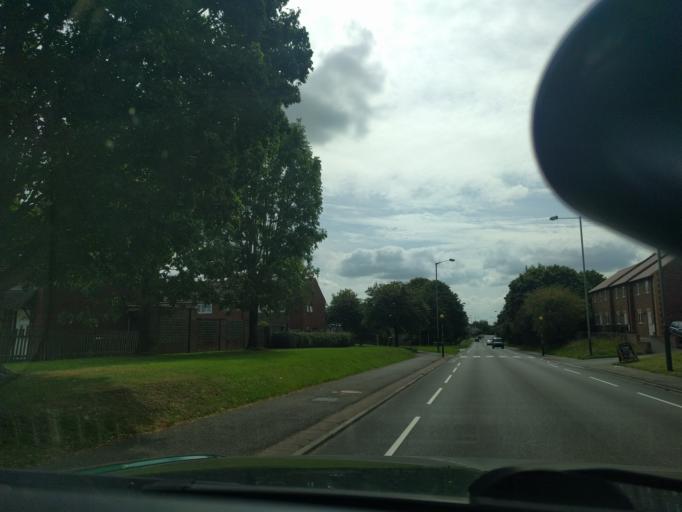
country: GB
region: England
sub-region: Wiltshire
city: Chippenham
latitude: 51.4630
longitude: -2.1380
